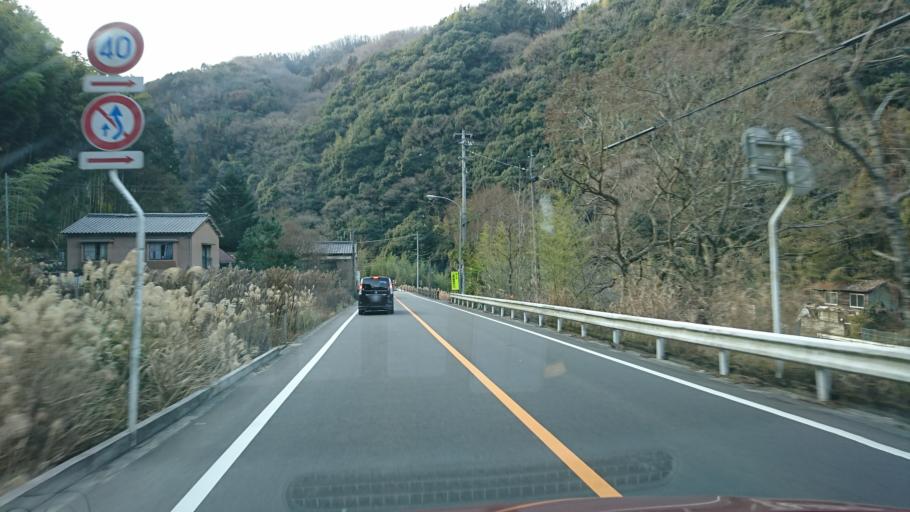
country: JP
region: Ehime
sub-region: Shikoku-chuo Shi
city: Matsuyama
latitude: 33.8961
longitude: 132.8459
